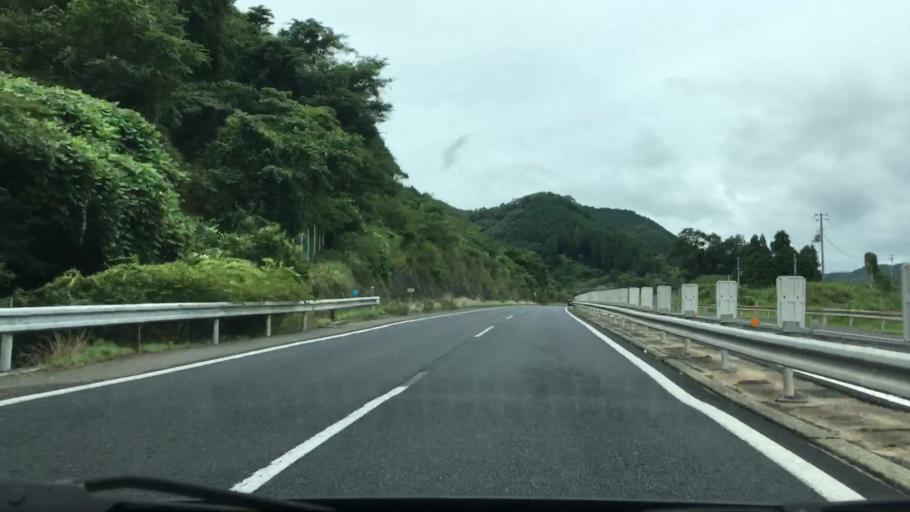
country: JP
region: Hyogo
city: Yamazakicho-nakabirose
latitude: 35.0105
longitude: 134.2982
